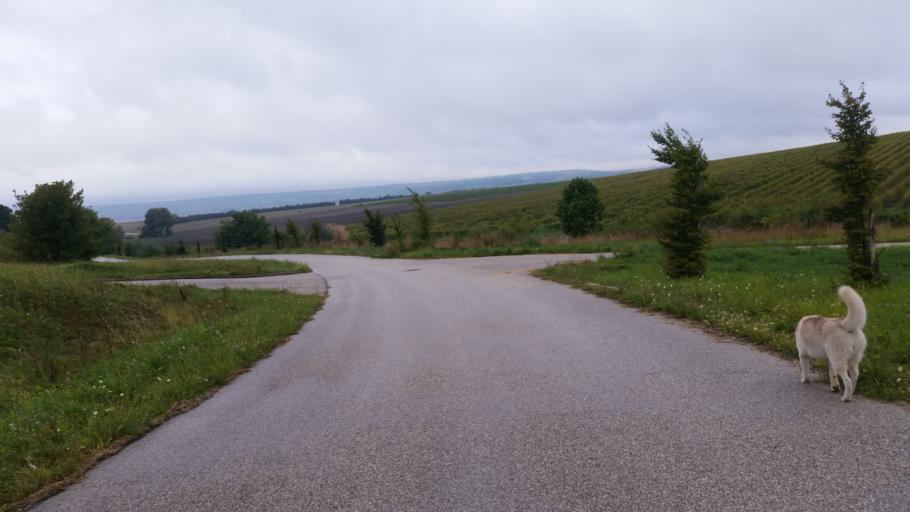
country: HU
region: Pest
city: Telki
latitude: 47.5643
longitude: 18.8095
